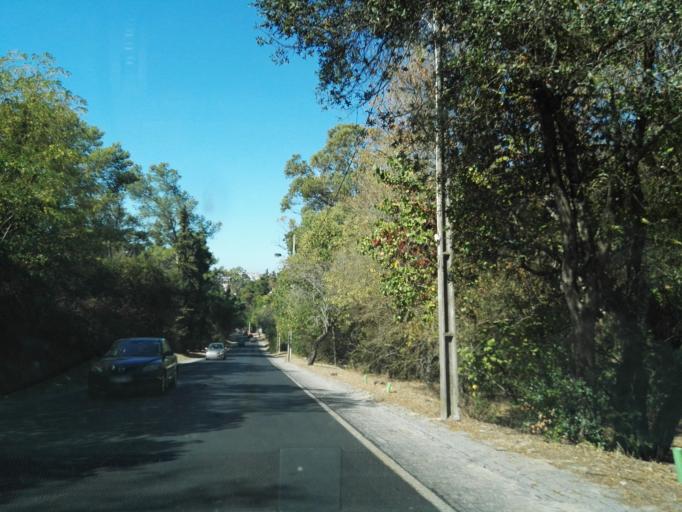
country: PT
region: Lisbon
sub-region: Odivelas
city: Pontinha
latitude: 38.7342
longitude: -9.1989
